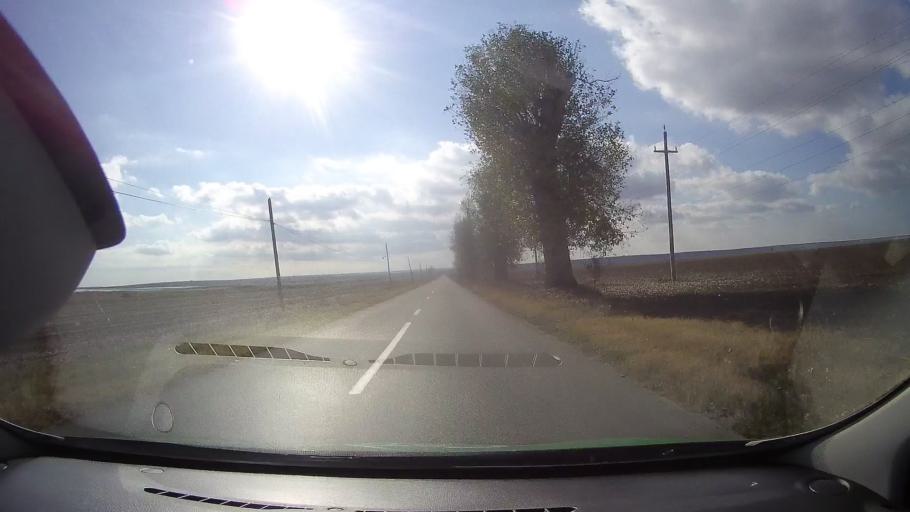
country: RO
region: Constanta
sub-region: Comuna Istria
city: Istria
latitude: 44.5425
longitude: 28.6906
